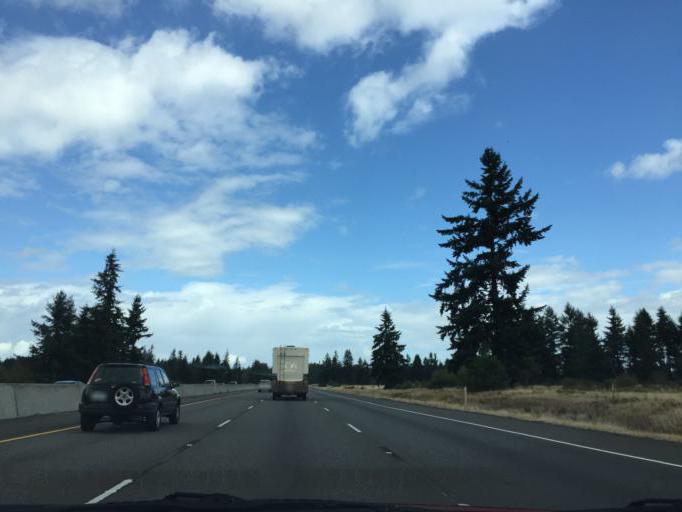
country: US
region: Washington
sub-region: Thurston County
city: Grand Mound
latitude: 46.8450
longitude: -122.9817
